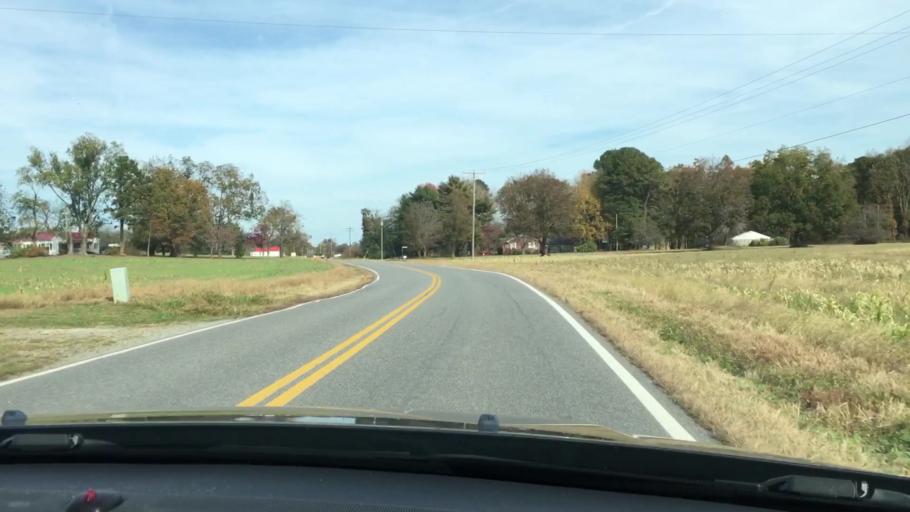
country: US
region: Virginia
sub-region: King William County
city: West Point
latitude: 37.4786
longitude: -76.8196
